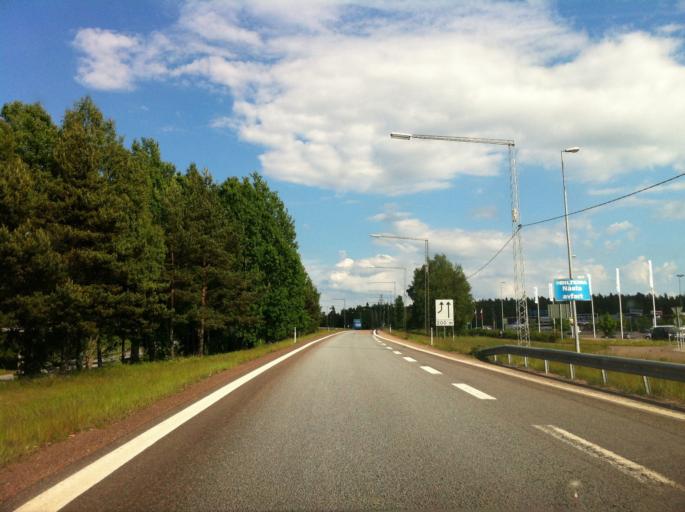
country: SE
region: Vaermland
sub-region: Hammaro Kommun
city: Skoghall
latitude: 59.3811
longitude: 13.4198
